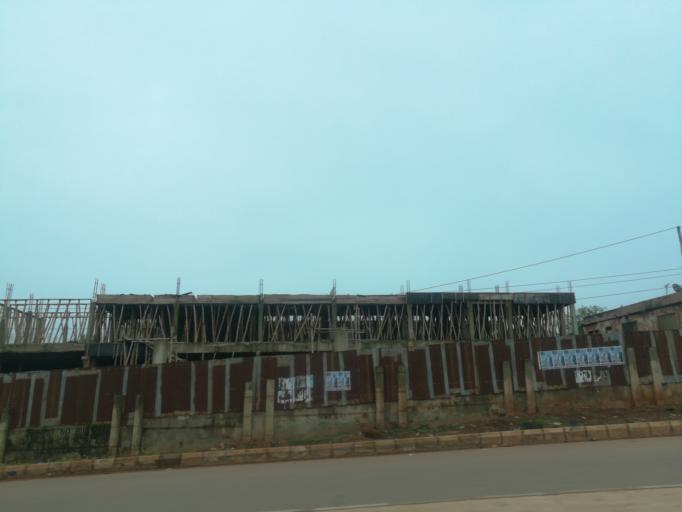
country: NG
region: Oyo
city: Ibadan
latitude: 7.3909
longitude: 3.9407
